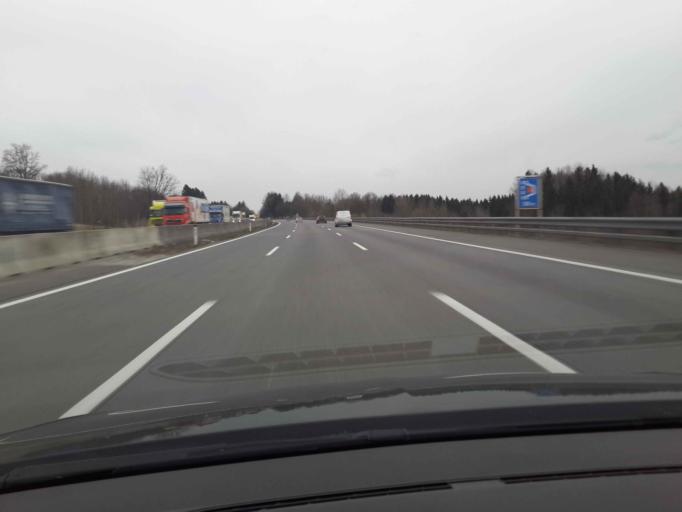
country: AT
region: Lower Austria
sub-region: Politischer Bezirk Amstetten
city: Sankt Georgen am Ybbsfelde
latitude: 48.1437
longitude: 14.9173
